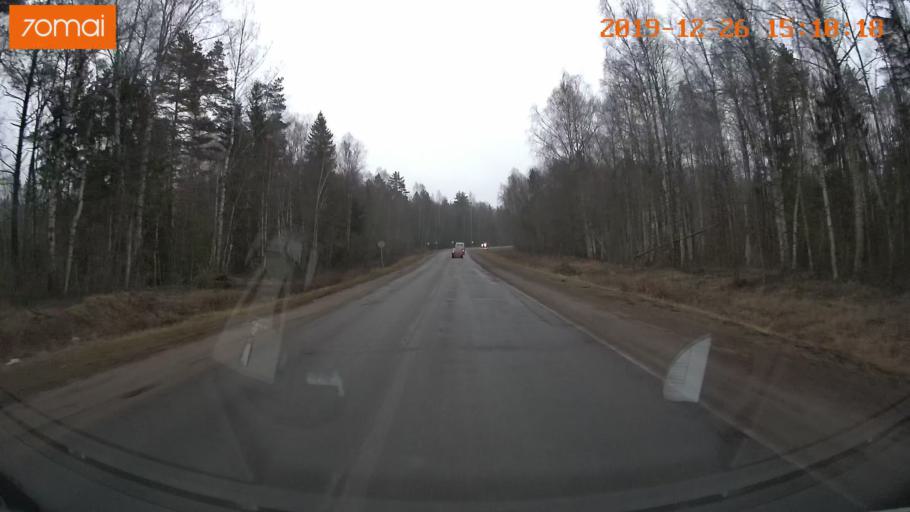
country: RU
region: Jaroslavl
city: Rybinsk
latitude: 58.1413
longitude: 38.8501
